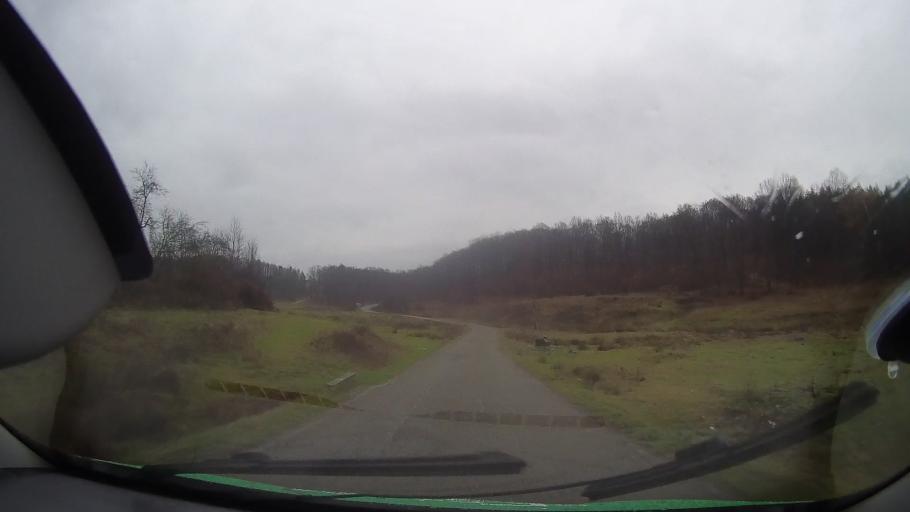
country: RO
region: Bihor
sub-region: Comuna Rabagani
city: Rabagani
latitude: 46.7208
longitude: 22.2320
